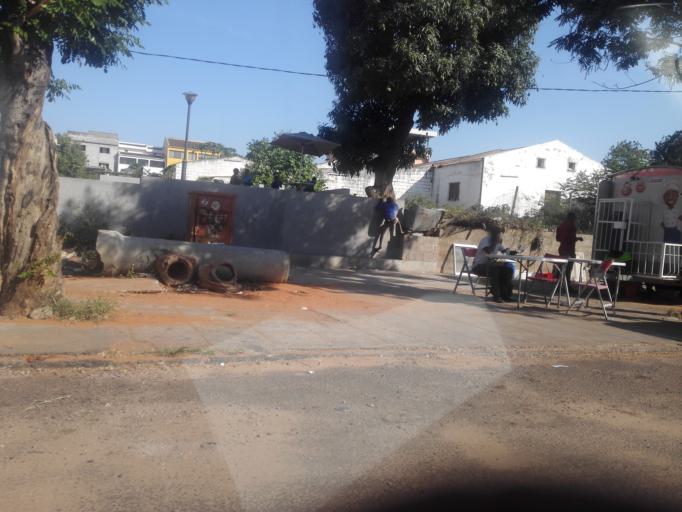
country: MZ
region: Maputo City
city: Maputo
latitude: -25.9539
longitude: 32.5880
